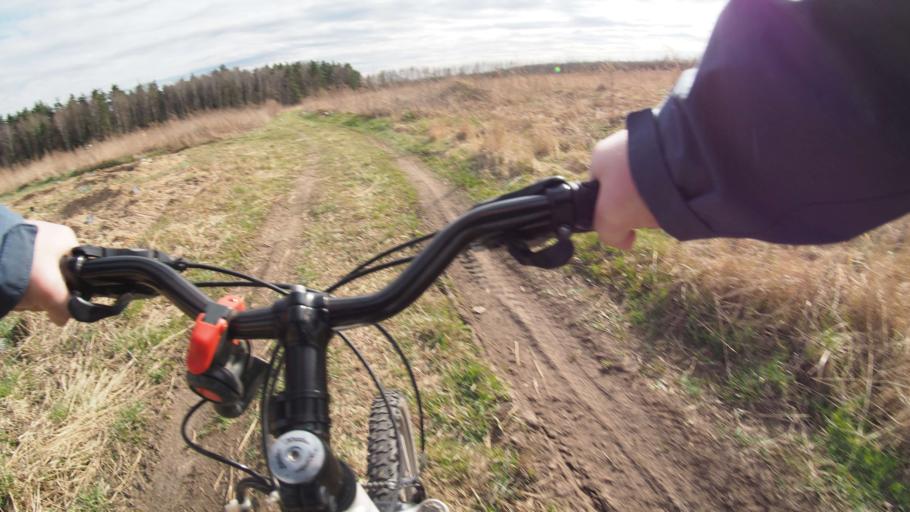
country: RU
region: Moskovskaya
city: Ramenskoye
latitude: 55.6006
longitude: 38.2894
